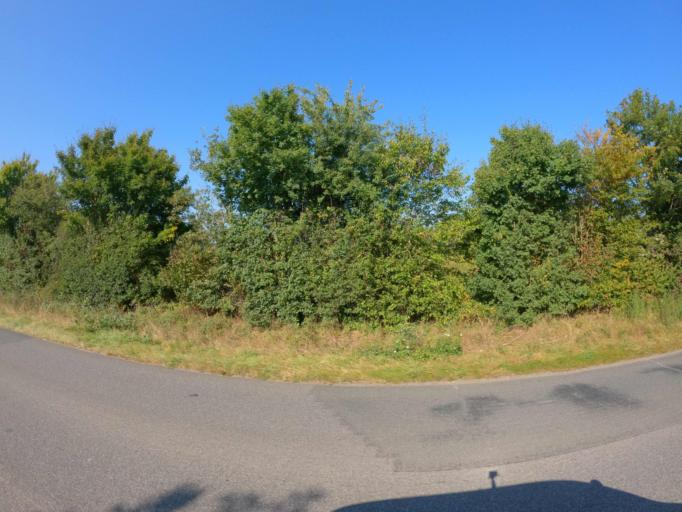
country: FR
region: Pays de la Loire
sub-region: Departement de la Loire-Atlantique
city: La Chevroliere
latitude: 47.0673
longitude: -1.5678
